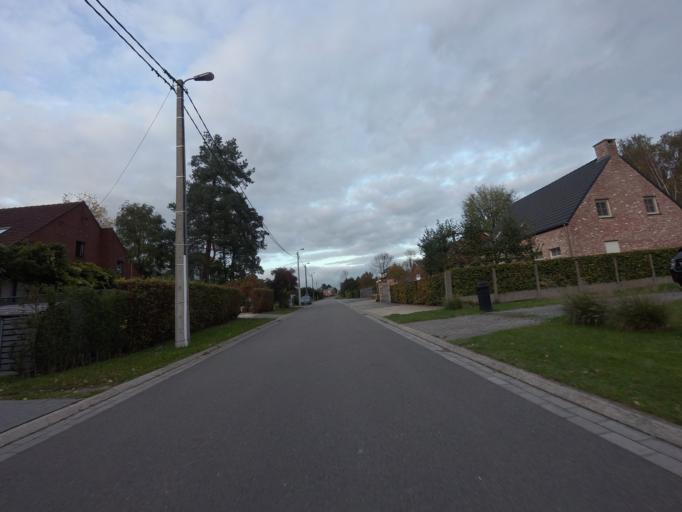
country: BE
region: Flanders
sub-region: Provincie Vlaams-Brabant
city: Steenokkerzeel
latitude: 50.9259
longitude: 4.5250
